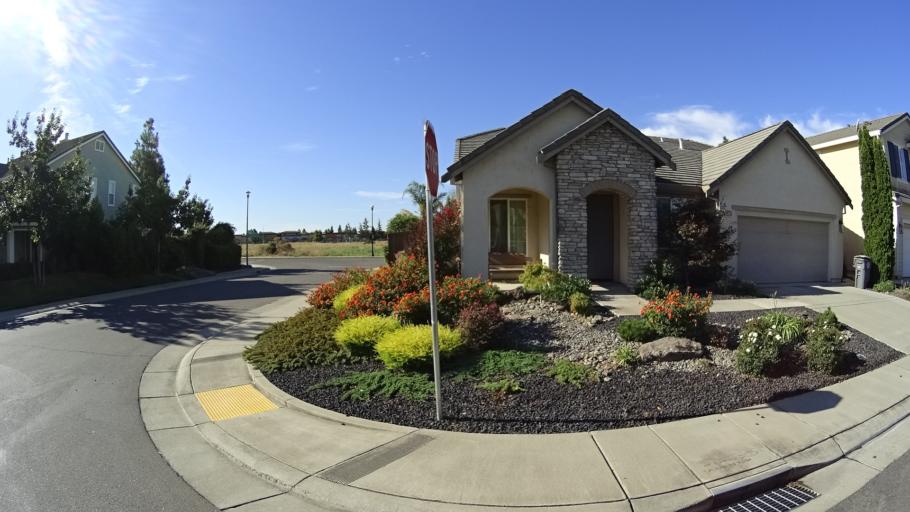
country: US
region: California
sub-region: Sacramento County
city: Laguna
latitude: 38.4112
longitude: -121.4807
